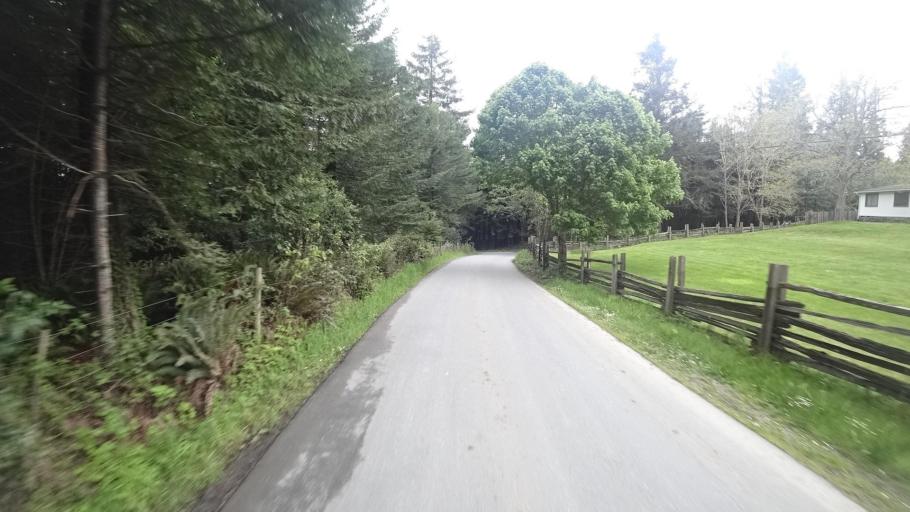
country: US
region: California
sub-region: Humboldt County
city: Blue Lake
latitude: 40.9075
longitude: -123.9739
